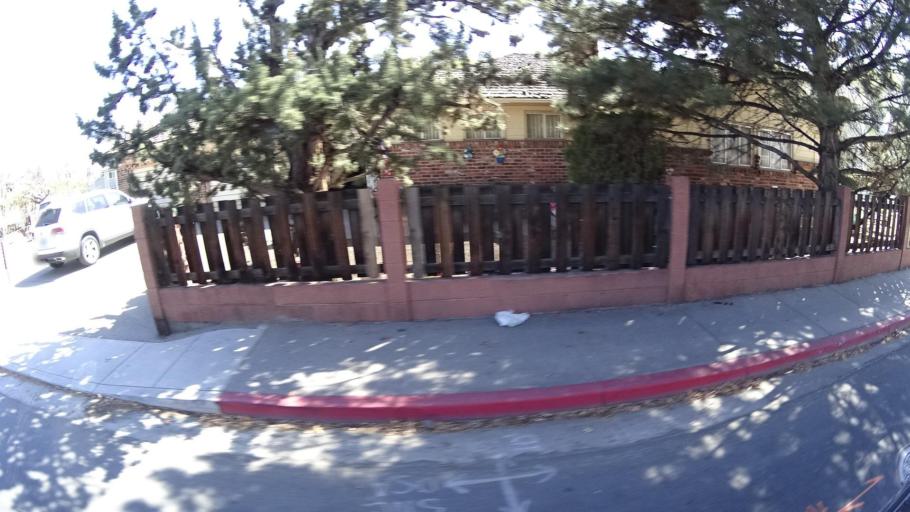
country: US
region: Nevada
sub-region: Washoe County
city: Reno
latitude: 39.5042
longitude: -119.8071
